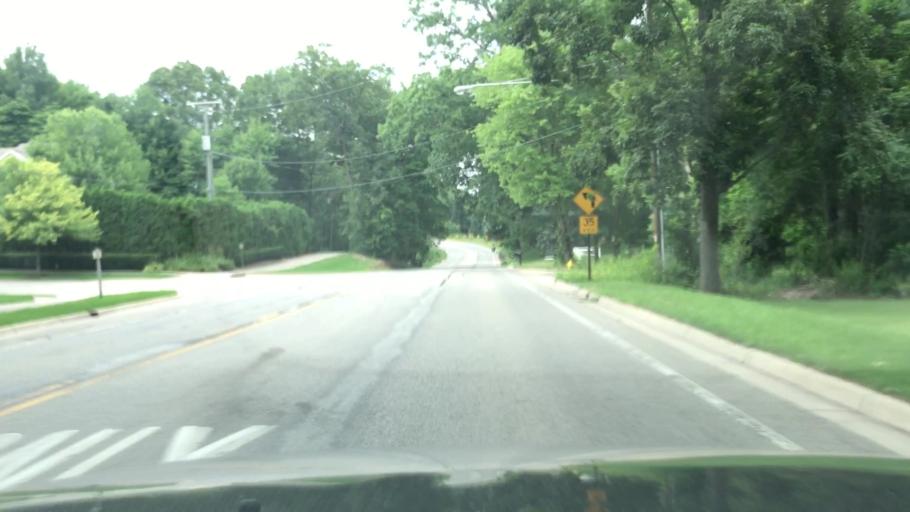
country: US
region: Michigan
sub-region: Kent County
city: East Grand Rapids
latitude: 42.9589
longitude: -85.5559
